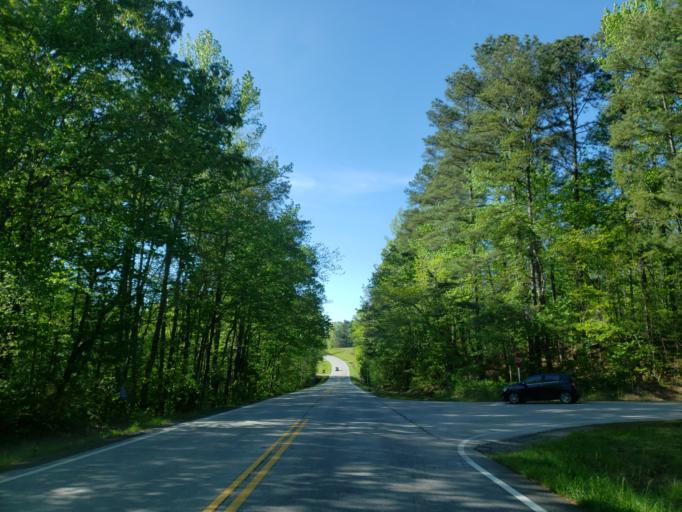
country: US
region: Georgia
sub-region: Haralson County
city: Tallapoosa
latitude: 33.8603
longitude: -85.2927
